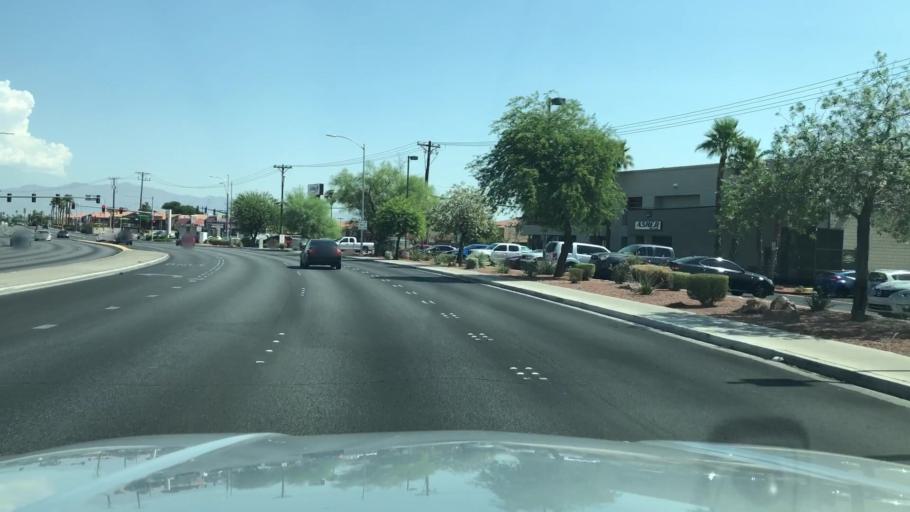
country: US
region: Nevada
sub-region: Clark County
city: Spring Valley
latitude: 36.1577
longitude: -115.2241
